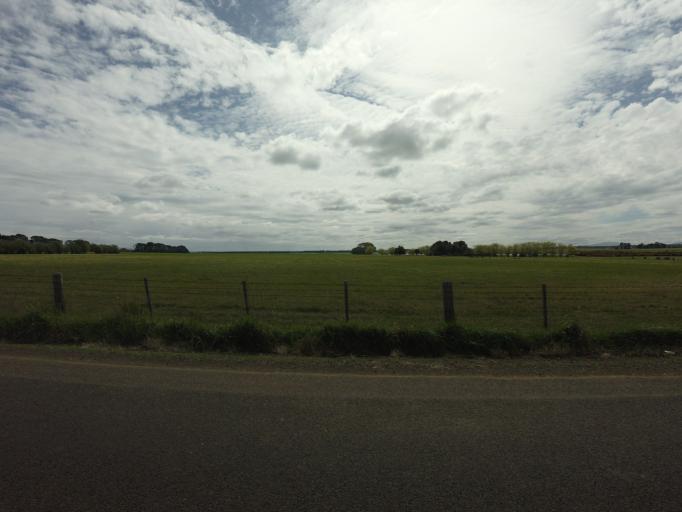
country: AU
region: Tasmania
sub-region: Northern Midlands
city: Longford
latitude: -41.7158
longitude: 147.1895
